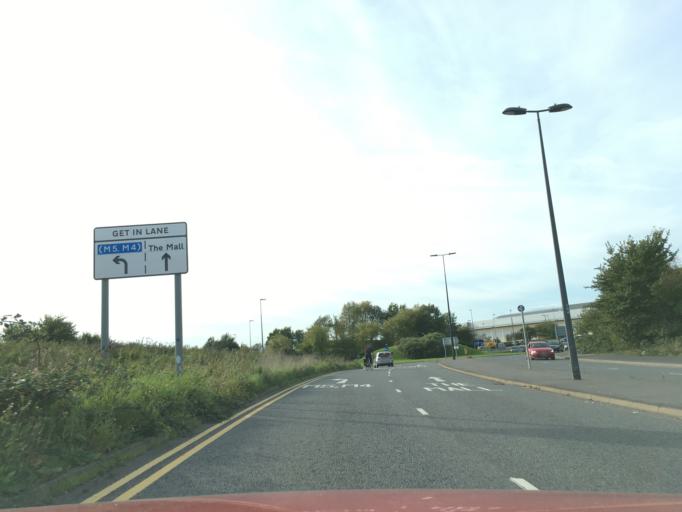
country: GB
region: England
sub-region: South Gloucestershire
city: Almondsbury
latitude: 51.5217
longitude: -2.5906
